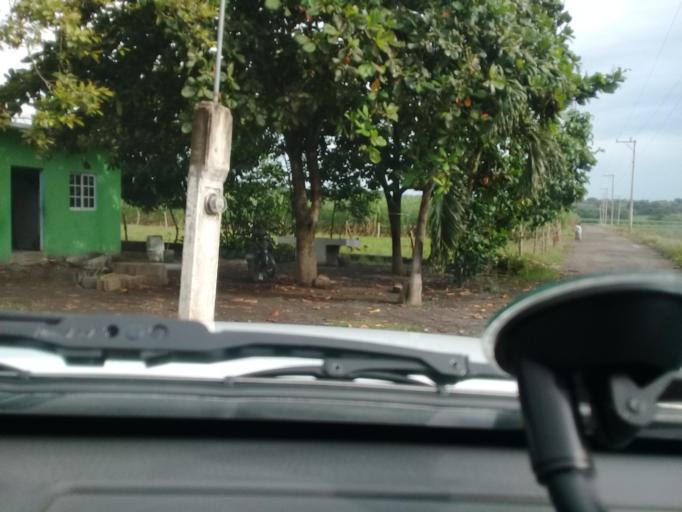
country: MX
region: Veracruz
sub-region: Puente Nacional
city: Cabezas
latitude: 19.3250
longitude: -96.3842
